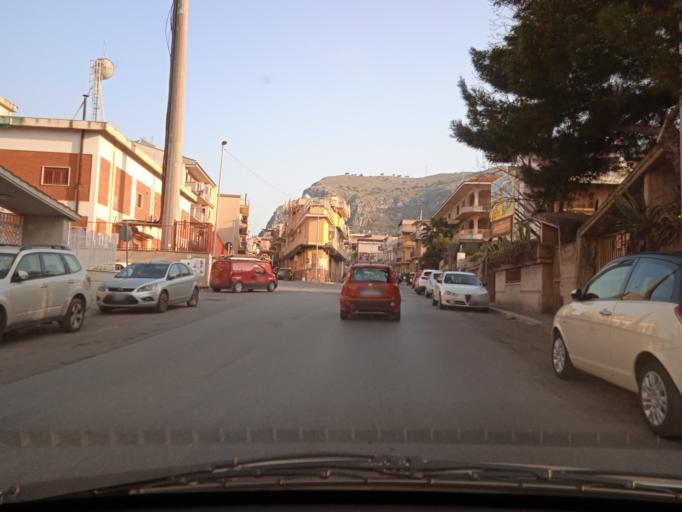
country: IT
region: Sicily
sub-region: Palermo
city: Villabate
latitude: 38.0774
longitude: 13.4387
